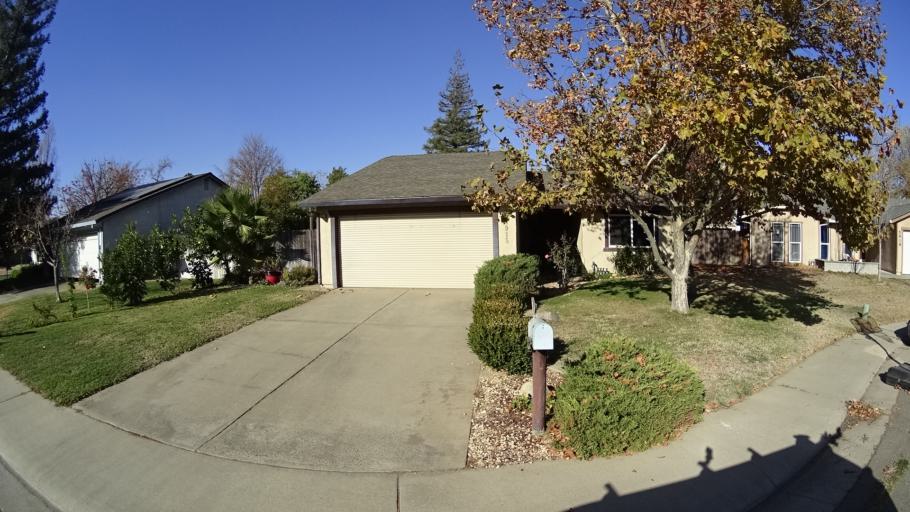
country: US
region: California
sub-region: Sacramento County
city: Antelope
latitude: 38.6942
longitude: -121.3256
